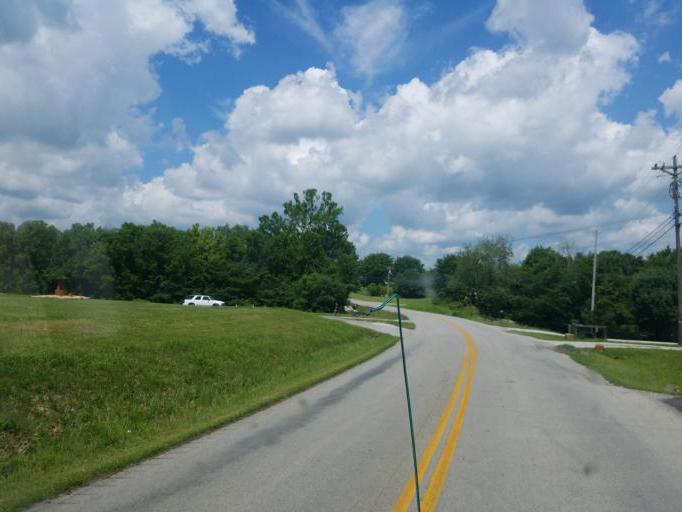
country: US
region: Kentucky
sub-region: Grayson County
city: Leitchfield
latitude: 37.5063
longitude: -86.3171
